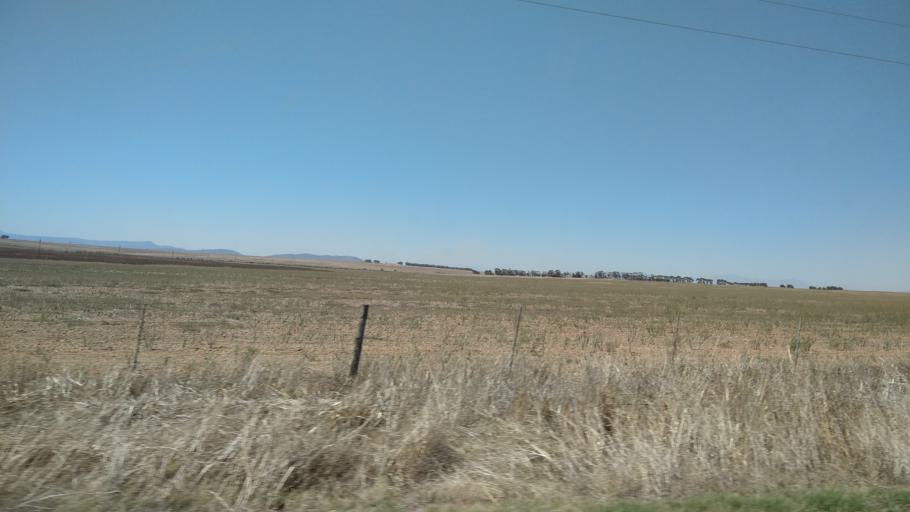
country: ZA
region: Western Cape
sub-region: West Coast District Municipality
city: Moorreesburg
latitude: -33.1726
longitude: 18.4836
